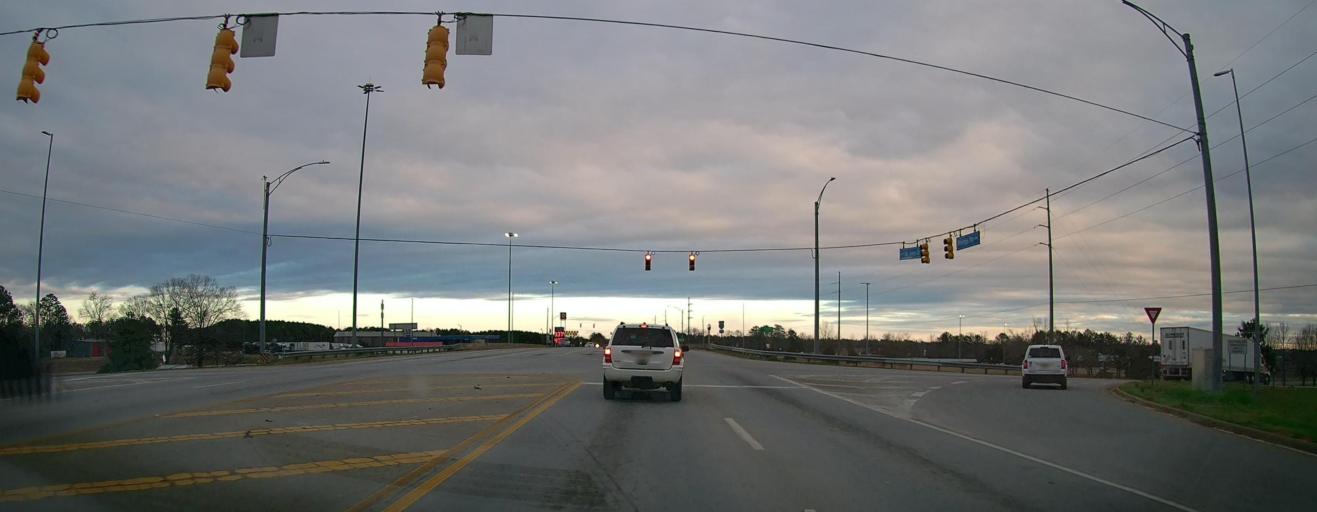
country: US
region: Alabama
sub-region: Chambers County
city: Huguley
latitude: 32.8229
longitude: -85.2145
